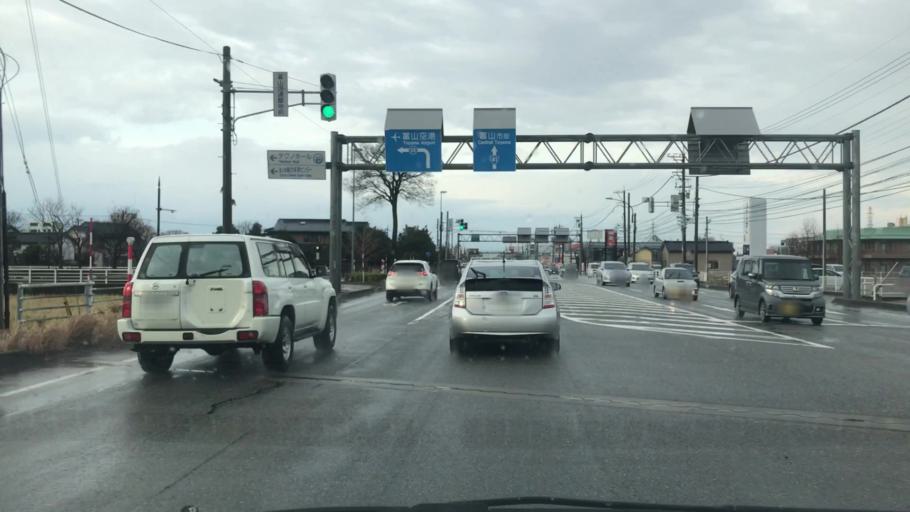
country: JP
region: Toyama
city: Toyama-shi
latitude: 36.6425
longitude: 137.2095
